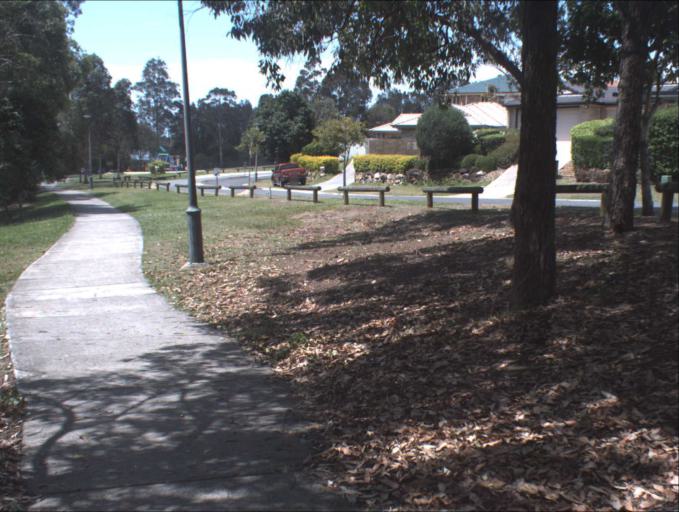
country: AU
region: Queensland
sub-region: Logan
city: Rochedale South
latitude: -27.6074
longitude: 153.1061
